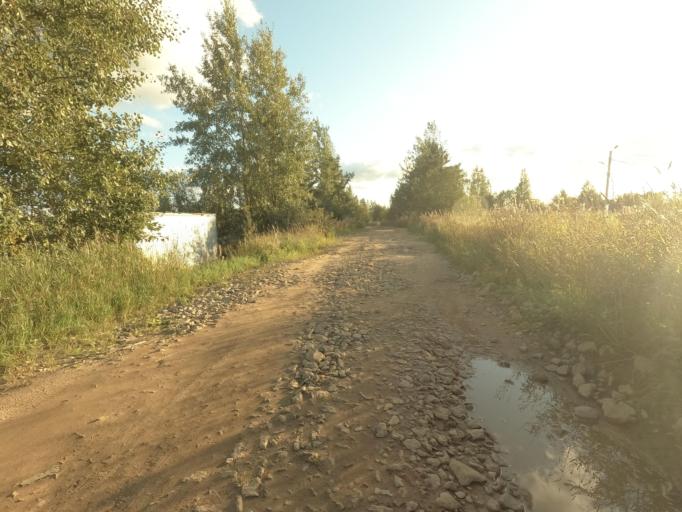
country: RU
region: Leningrad
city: Otradnoye
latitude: 59.8586
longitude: 30.7984
